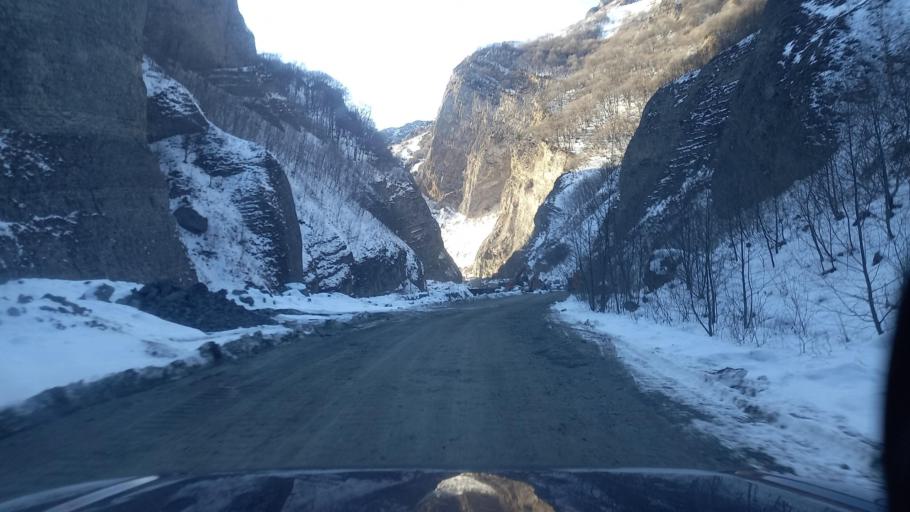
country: RU
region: Ingushetiya
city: Dzhayrakh
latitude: 42.8709
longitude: 44.5207
